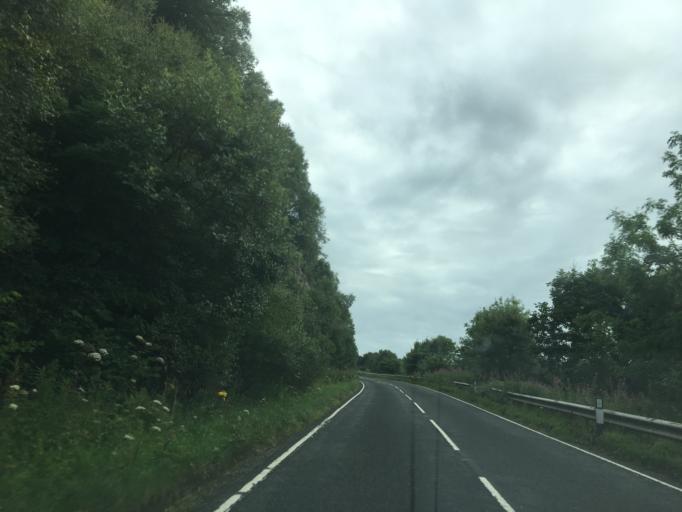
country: GB
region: Scotland
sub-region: Argyll and Bute
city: Oban
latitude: 56.3428
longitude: -5.5112
